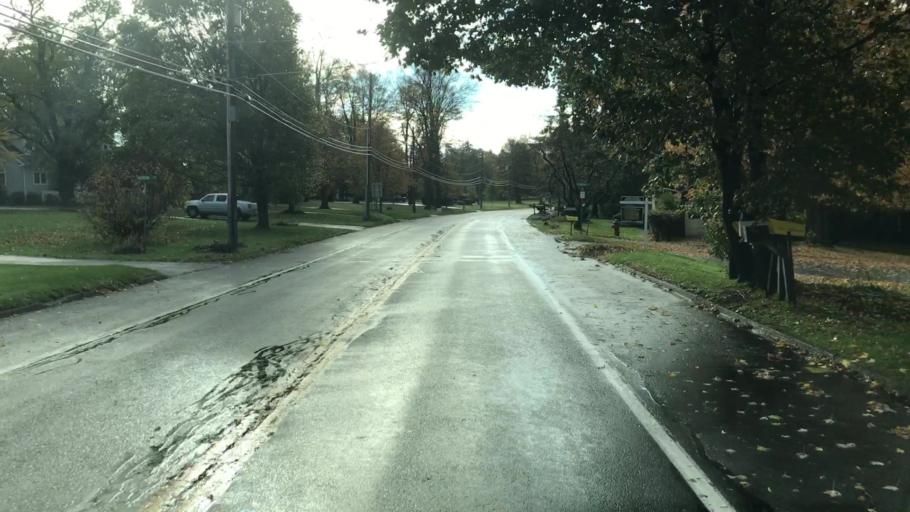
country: US
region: New York
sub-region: Onondaga County
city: Skaneateles
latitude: 42.9407
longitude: -76.4128
